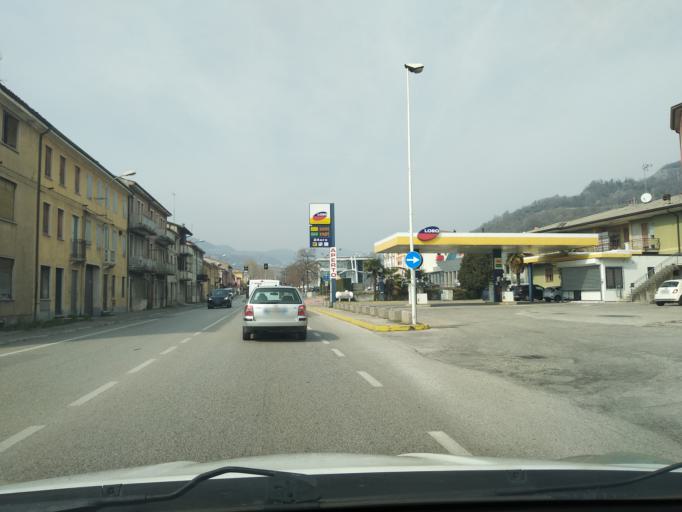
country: IT
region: Veneto
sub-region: Provincia di Vicenza
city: Chiampo
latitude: 45.5394
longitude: 11.2906
